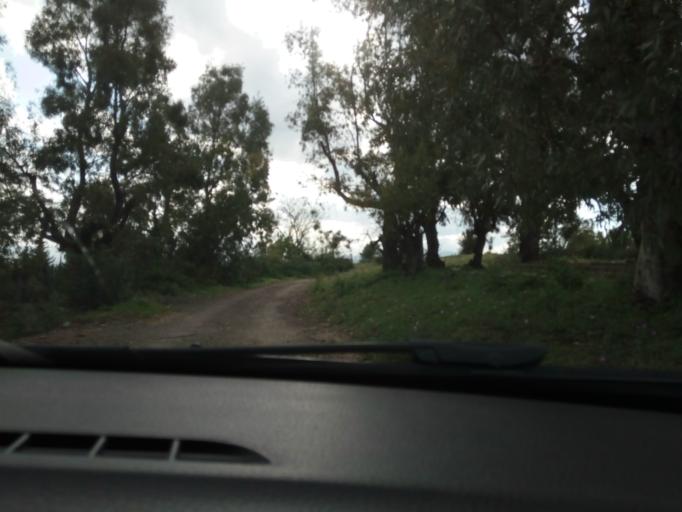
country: DZ
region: Tipaza
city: El Affroun
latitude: 36.3741
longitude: 2.5183
